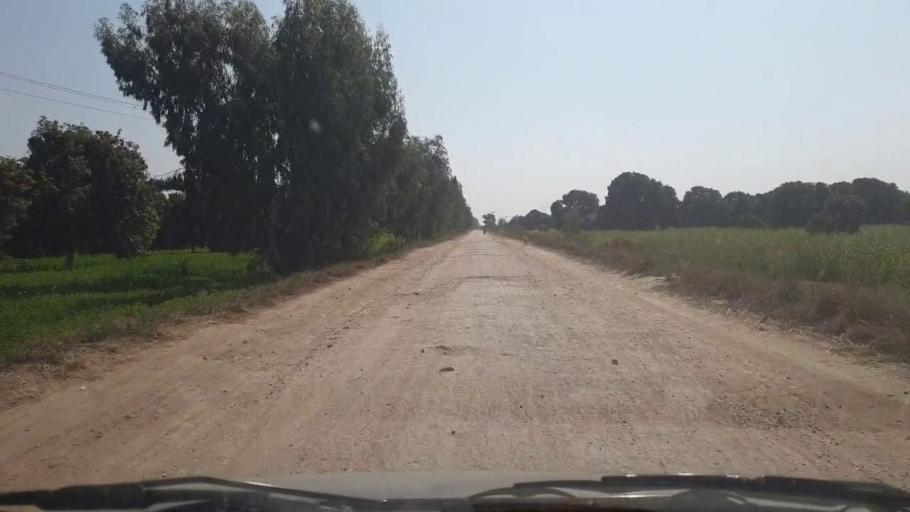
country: PK
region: Sindh
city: Samaro
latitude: 25.2685
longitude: 69.3471
